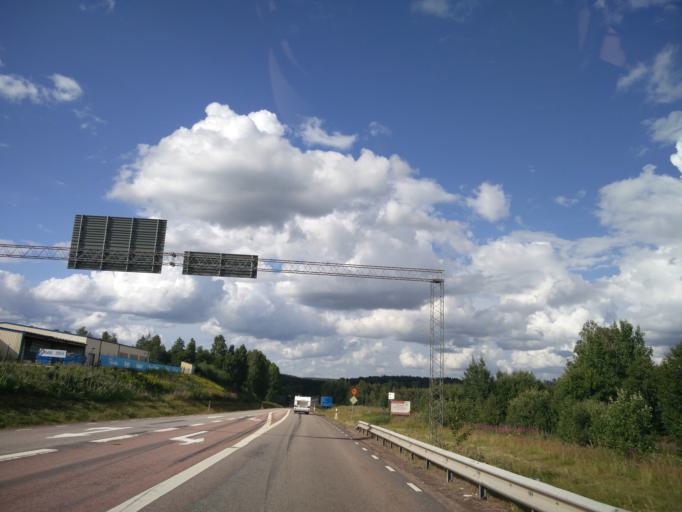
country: SE
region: Vaermland
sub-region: Torsby Kommun
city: Torsby
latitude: 60.1507
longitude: 13.0014
